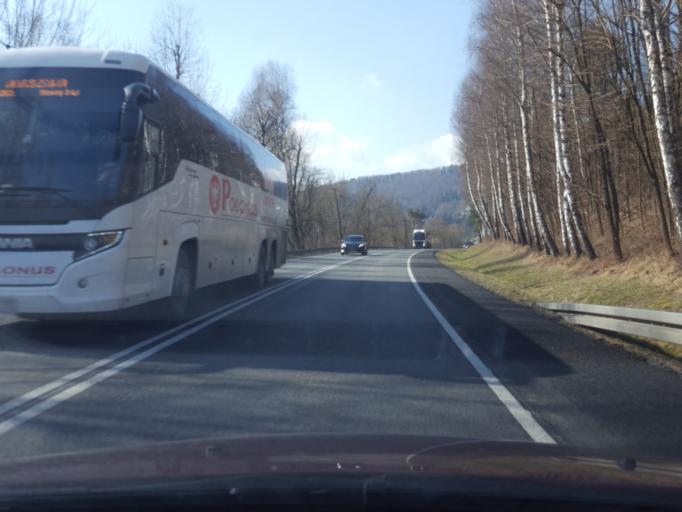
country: PL
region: Lesser Poland Voivodeship
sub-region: Powiat nowosadecki
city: Lososina Dolna
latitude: 49.7855
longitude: 20.6483
